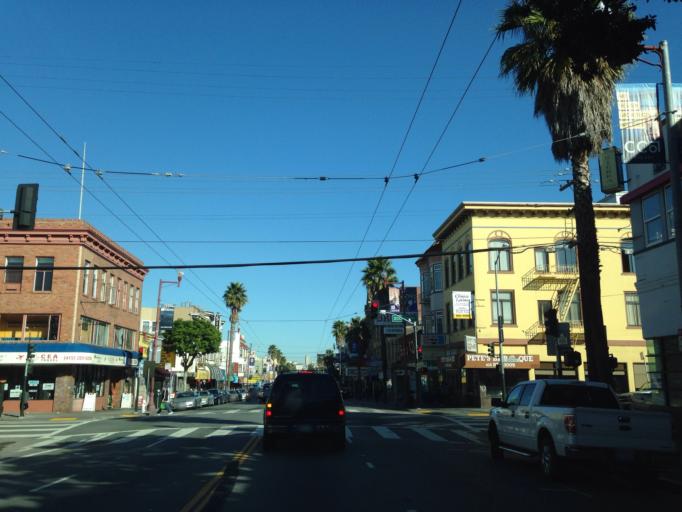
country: US
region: California
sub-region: San Francisco County
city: San Francisco
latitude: 37.7583
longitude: -122.4191
